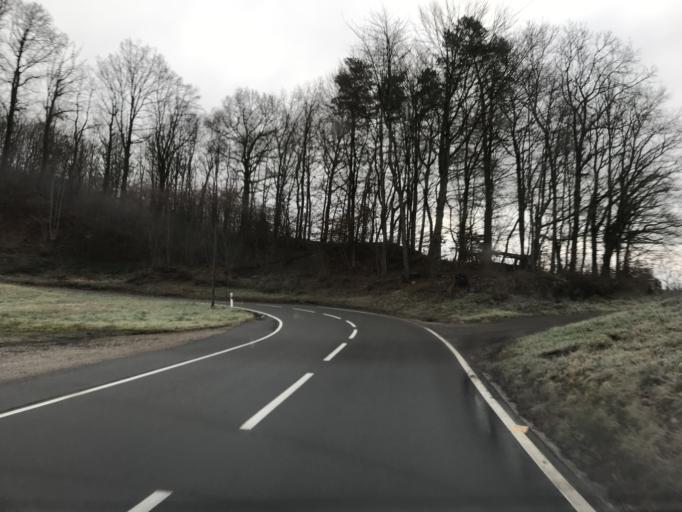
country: DE
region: Baden-Wuerttemberg
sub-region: Freiburg Region
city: Wehr
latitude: 47.6226
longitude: 7.9179
